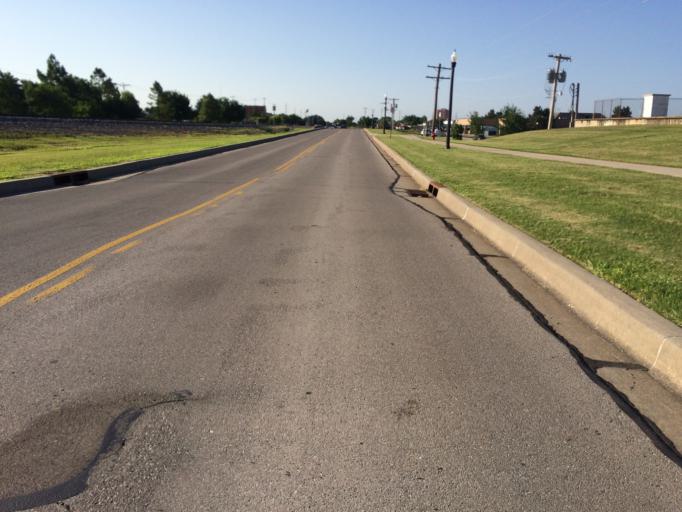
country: US
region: Oklahoma
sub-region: Cleveland County
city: Norman
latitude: 35.2249
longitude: -97.4464
